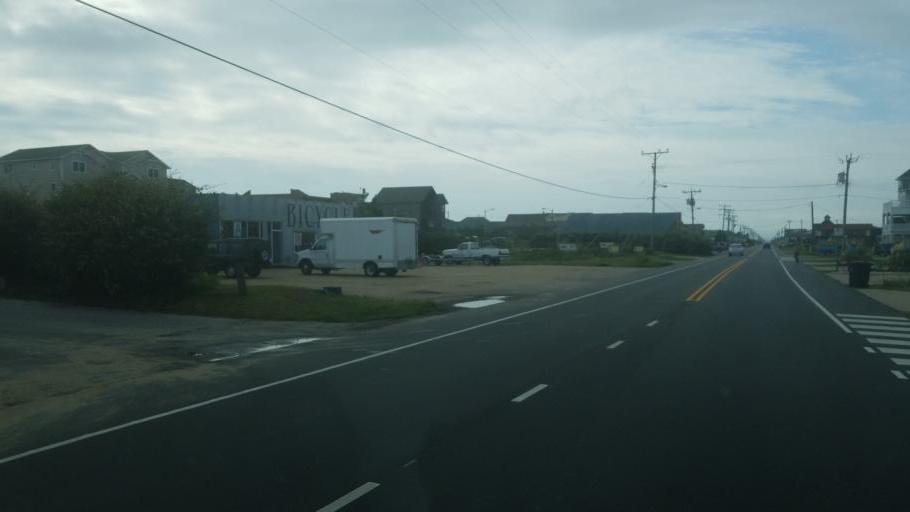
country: US
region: North Carolina
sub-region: Dare County
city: Kill Devil Hills
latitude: 36.0141
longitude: -75.6574
